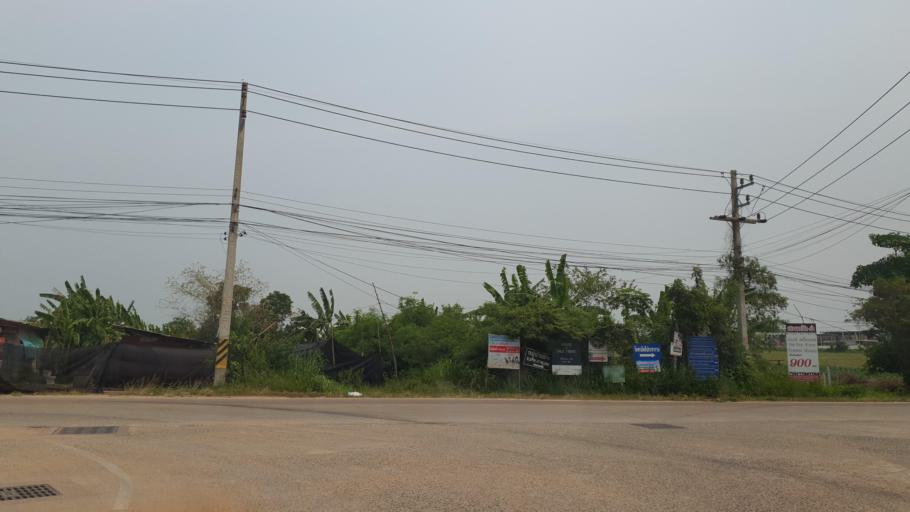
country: TH
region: Chon Buri
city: Phatthaya
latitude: 12.8935
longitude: 100.9282
